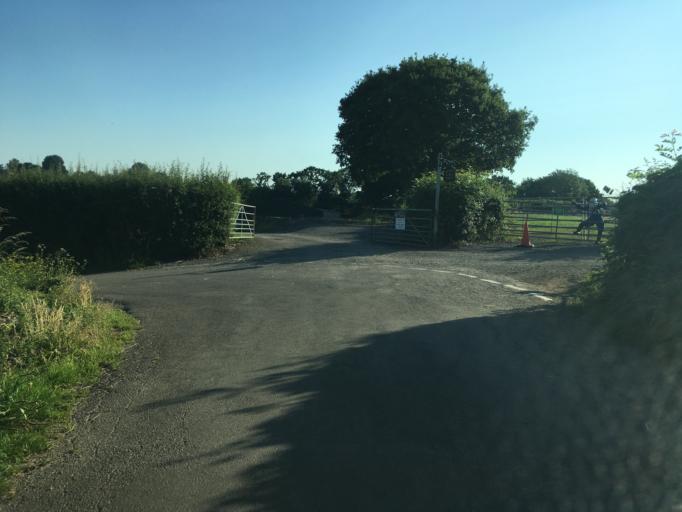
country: GB
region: England
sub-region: South Gloucestershire
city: Winterbourne
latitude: 51.5261
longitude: -2.4916
